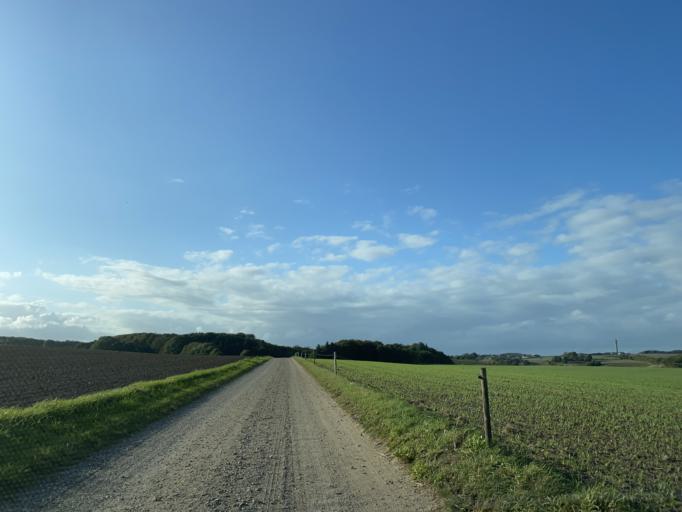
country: DK
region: Central Jutland
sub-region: Skanderborg Kommune
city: Ry
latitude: 56.1576
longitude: 9.8055
